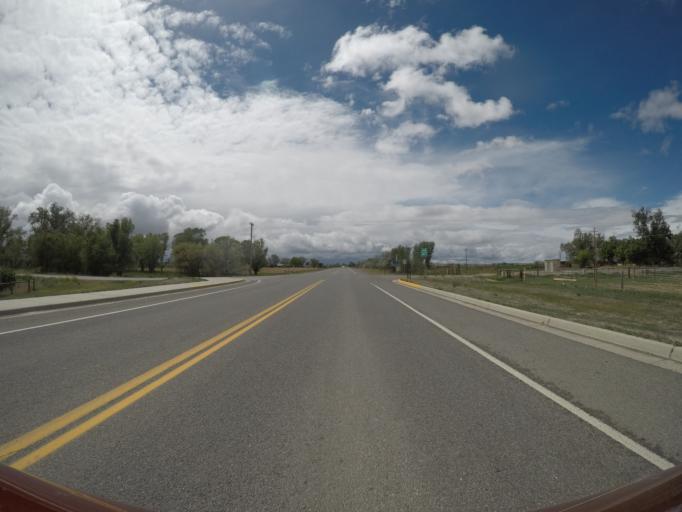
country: US
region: Wyoming
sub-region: Big Horn County
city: Lovell
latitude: 44.8839
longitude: -108.4775
